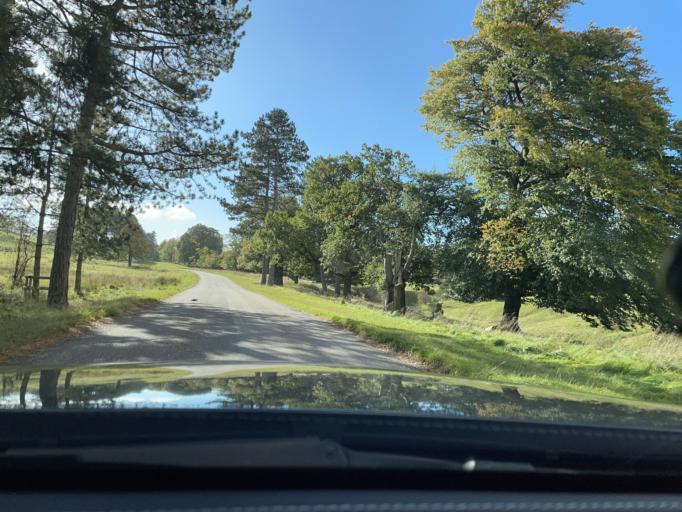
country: GB
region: England
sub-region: Cheshire East
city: Disley
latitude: 53.3470
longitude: -2.0569
